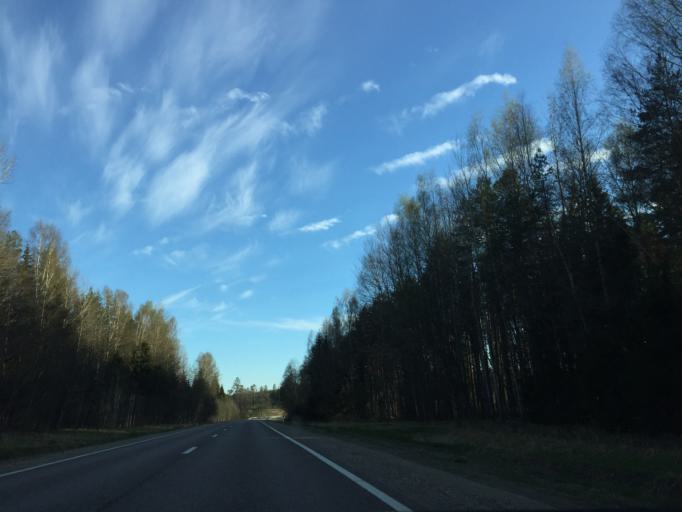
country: LV
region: Valkas Rajons
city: Valka
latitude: 57.7189
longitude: 25.9337
